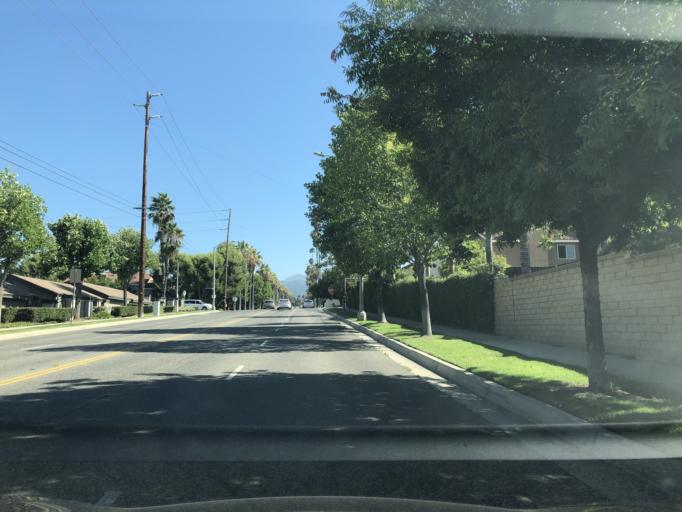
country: US
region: California
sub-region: Riverside County
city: El Cerrito
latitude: 33.8548
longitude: -117.5447
